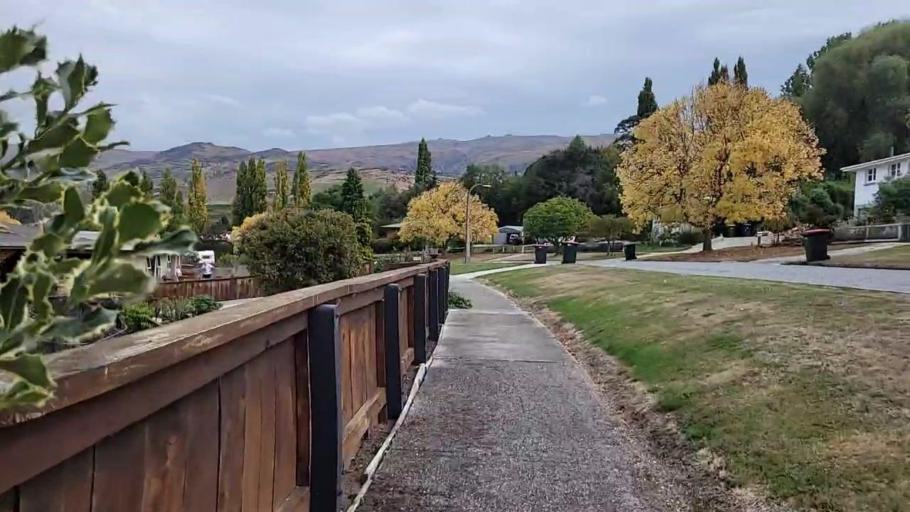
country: NZ
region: Otago
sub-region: Queenstown-Lakes District
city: Kingston
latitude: -45.4778
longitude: 169.3145
